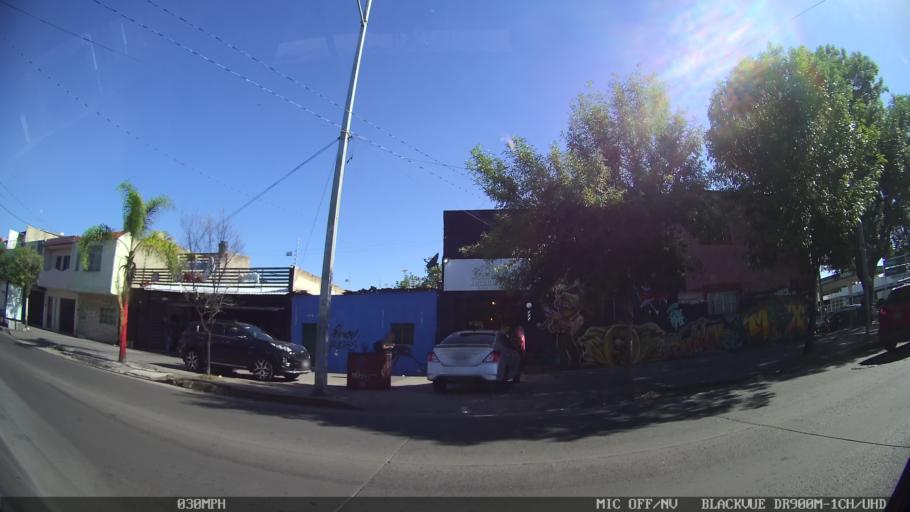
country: MX
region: Jalisco
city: Tlaquepaque
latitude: 20.6651
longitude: -103.3054
